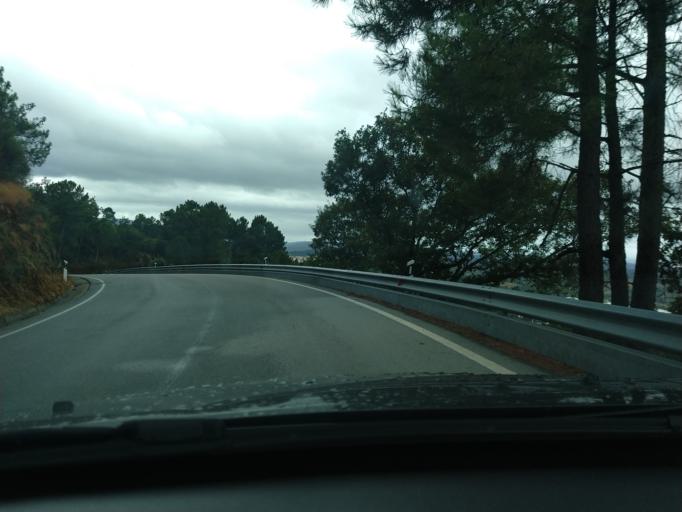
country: PT
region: Guarda
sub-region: Seia
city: Seia
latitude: 40.4136
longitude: -7.6952
